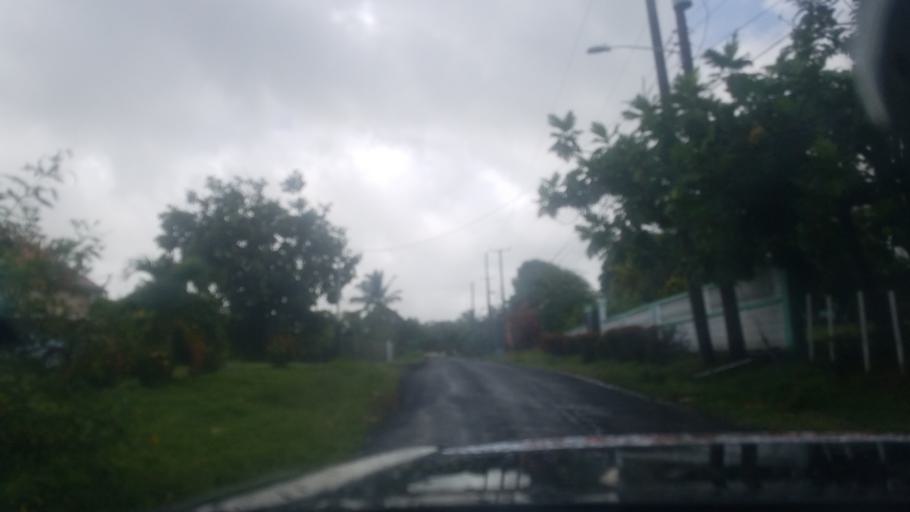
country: LC
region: Laborie Quarter
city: Laborie
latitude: 13.7473
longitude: -60.9683
